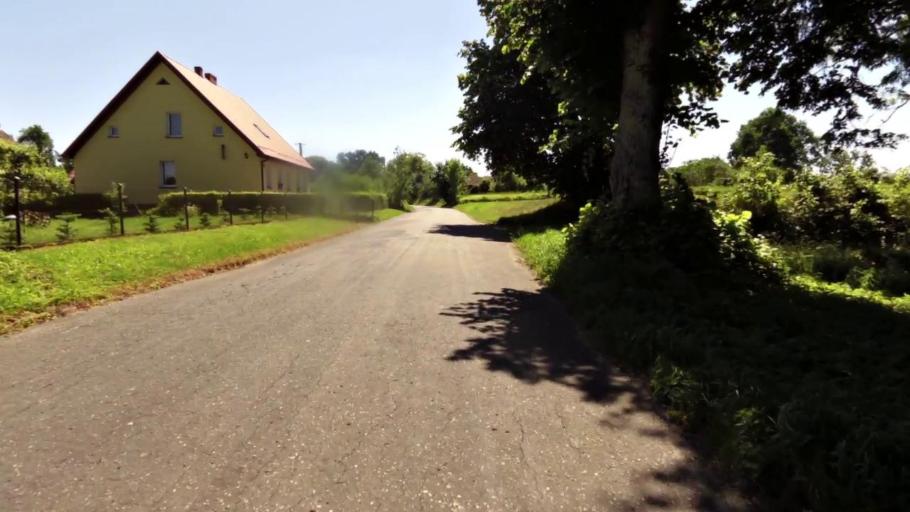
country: PL
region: West Pomeranian Voivodeship
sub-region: Powiat swidwinski
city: Polczyn-Zdroj
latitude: 53.8998
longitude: 16.0864
